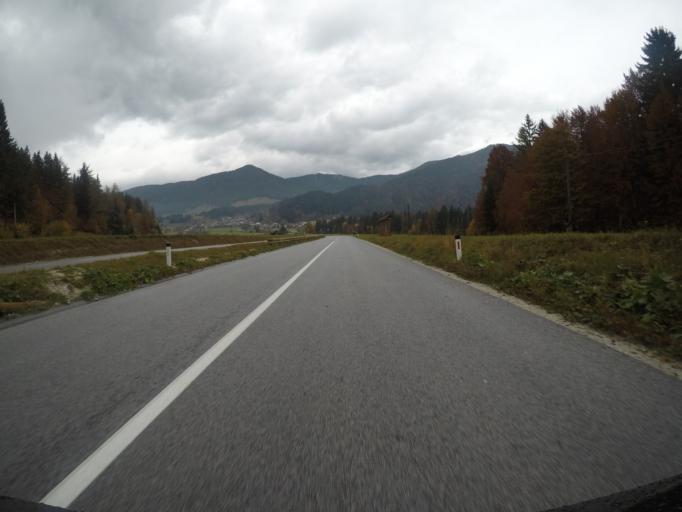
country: SI
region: Kranjska Gora
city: Kranjska Gora
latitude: 46.4865
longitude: 13.7245
